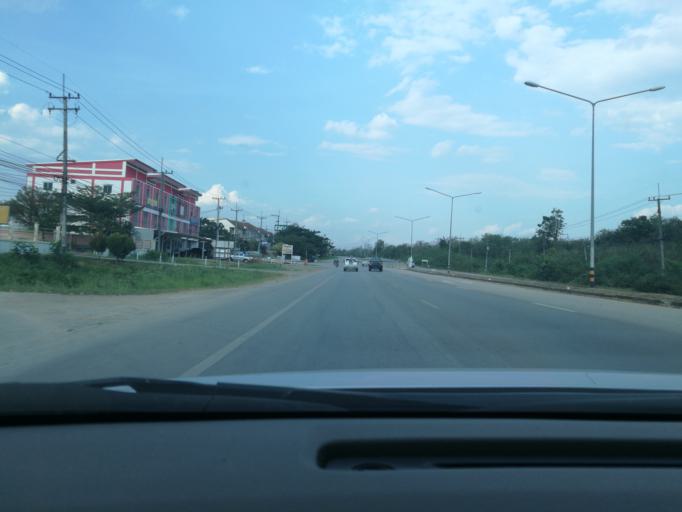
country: TH
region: Phetchabun
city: Phetchabun
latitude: 16.4687
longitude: 101.1580
